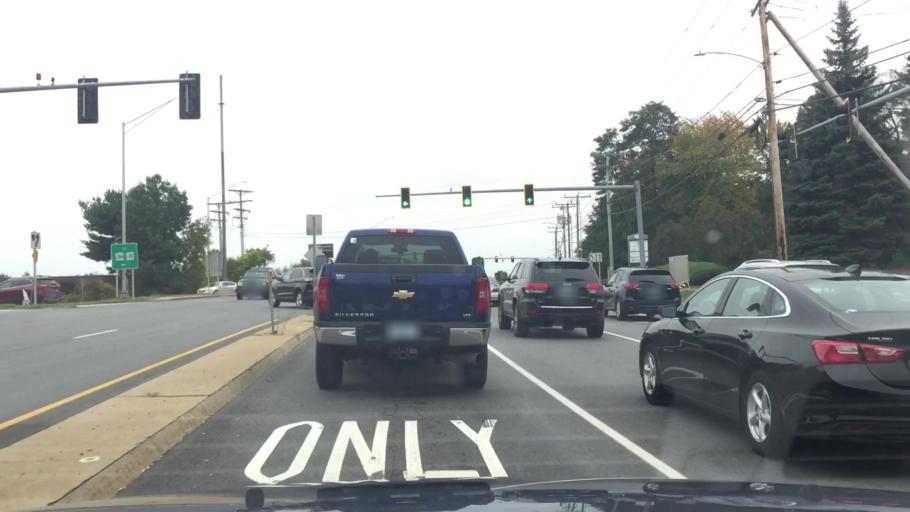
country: US
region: New Hampshire
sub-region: Hillsborough County
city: Hudson
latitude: 42.7210
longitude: -71.4430
